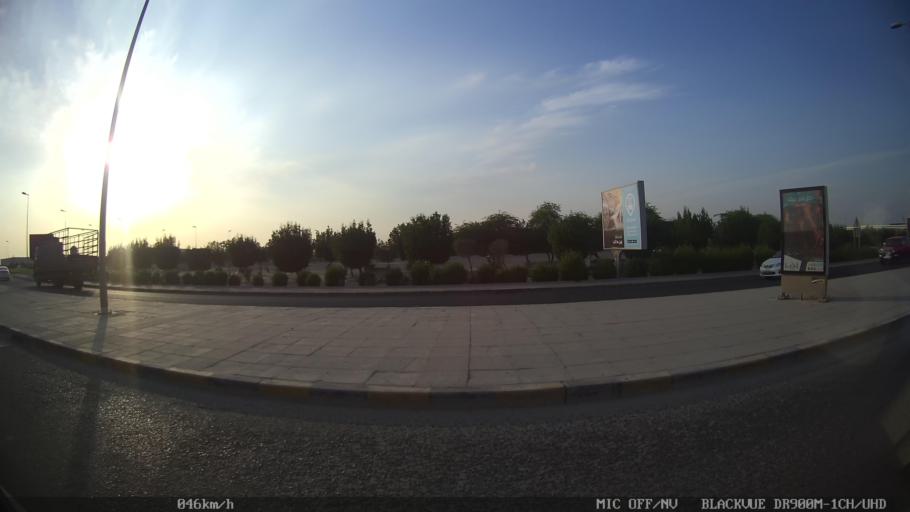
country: KW
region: Al Farwaniyah
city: Janub as Surrah
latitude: 29.2580
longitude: 48.0122
